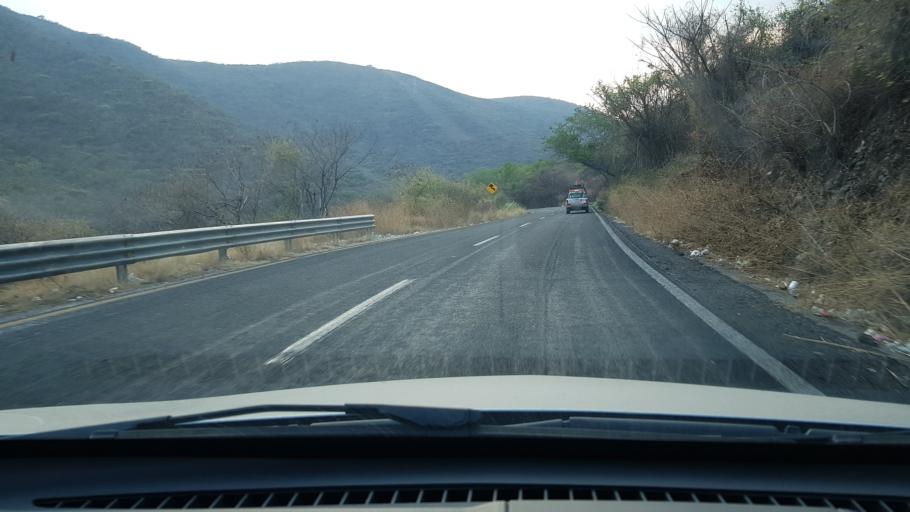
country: MX
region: Morelos
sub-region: Jiutepec
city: Independencia
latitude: 18.8562
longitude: -99.1105
